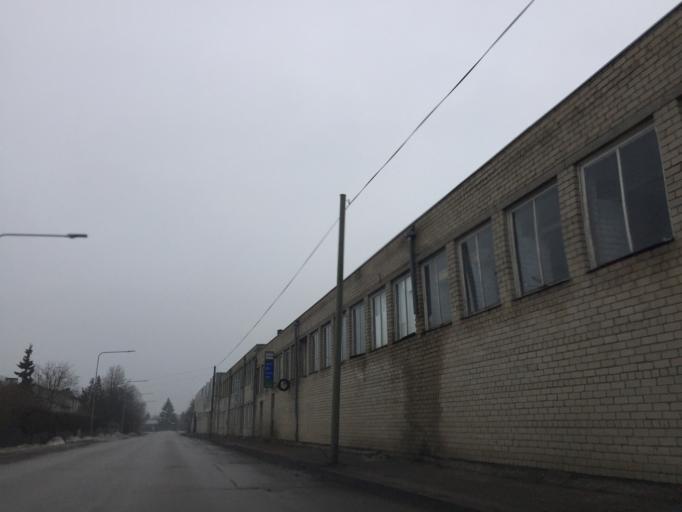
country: EE
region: Saare
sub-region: Kuressaare linn
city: Kuressaare
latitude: 58.2522
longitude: 22.4995
